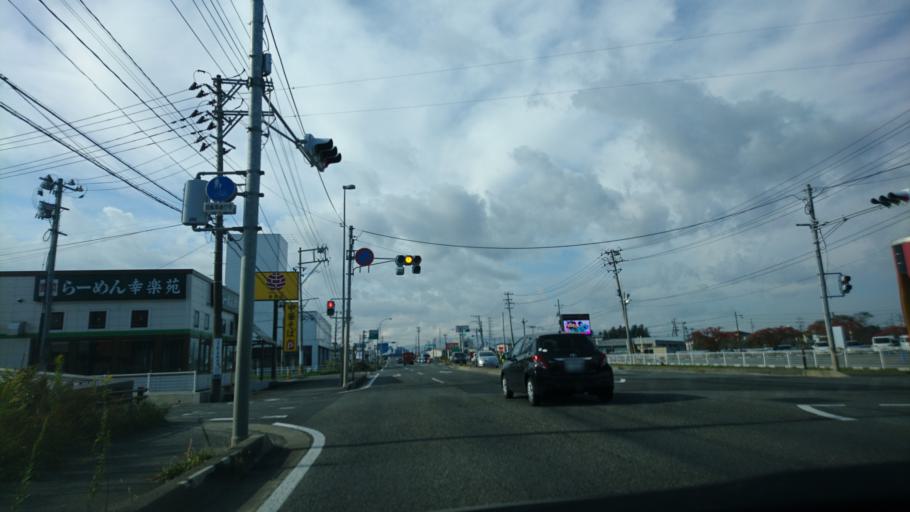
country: JP
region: Miyagi
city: Furukawa
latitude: 38.5873
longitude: 140.9516
